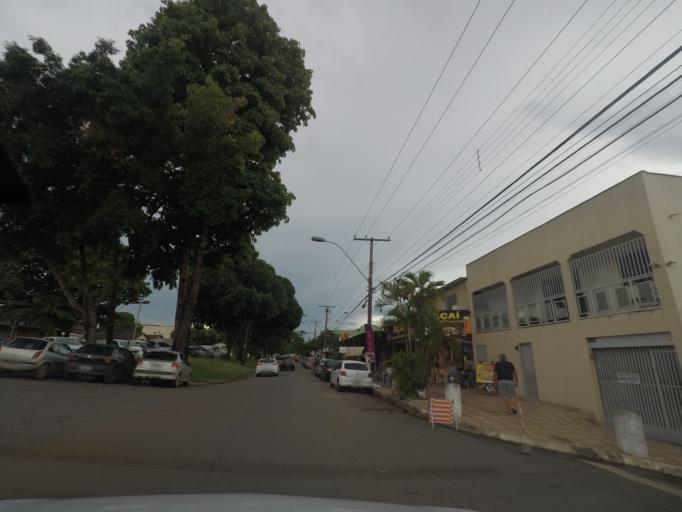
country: BR
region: Goias
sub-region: Goiania
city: Goiania
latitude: -16.7176
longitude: -49.2418
